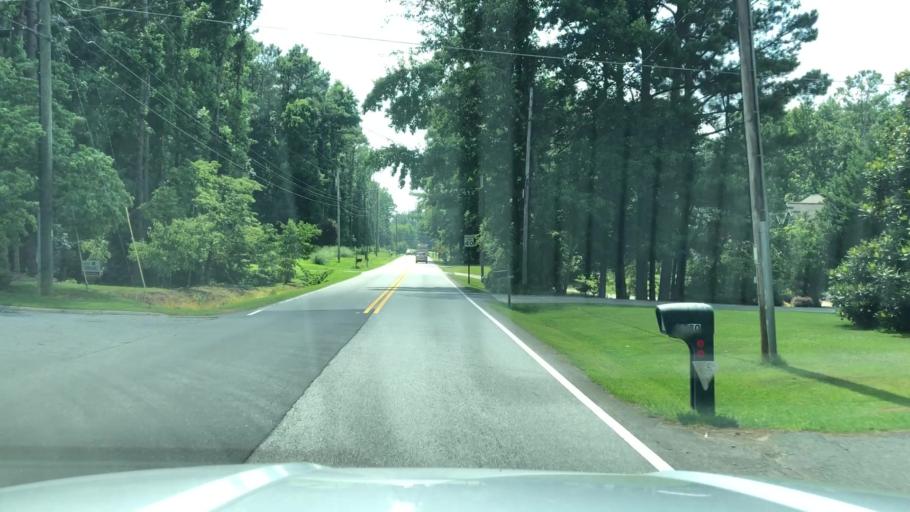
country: US
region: Georgia
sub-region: Cobb County
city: Acworth
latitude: 33.9740
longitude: -84.7210
